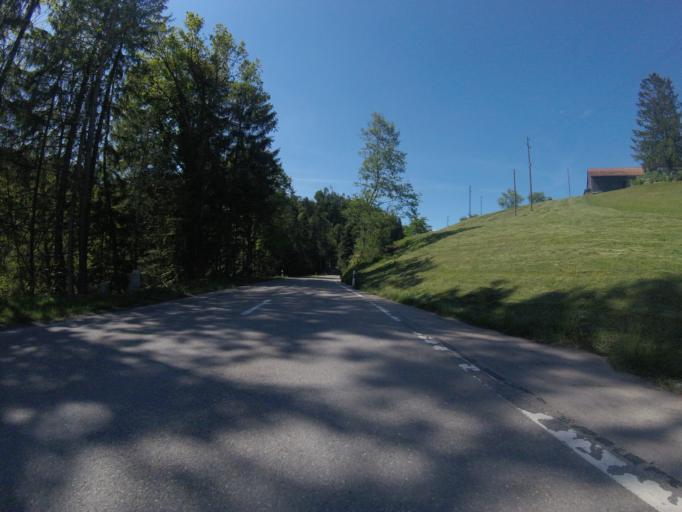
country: CH
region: Saint Gallen
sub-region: Wahlkreis Toggenburg
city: Mogelsberg
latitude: 47.3714
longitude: 9.1222
